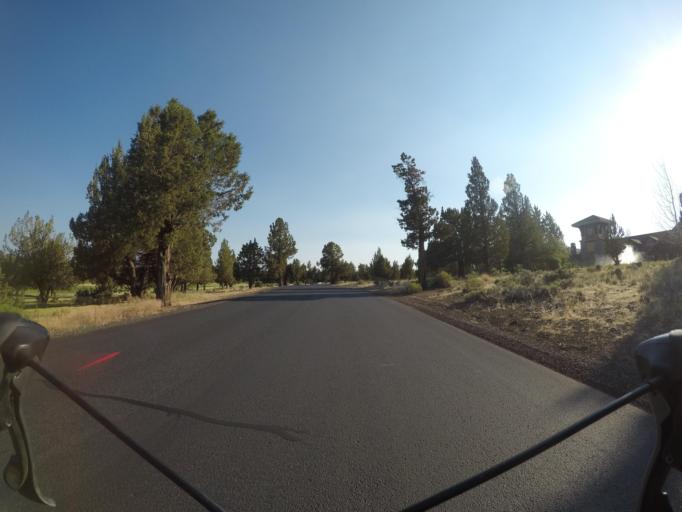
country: US
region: Oregon
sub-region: Deschutes County
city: Redmond
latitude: 44.2628
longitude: -121.2614
